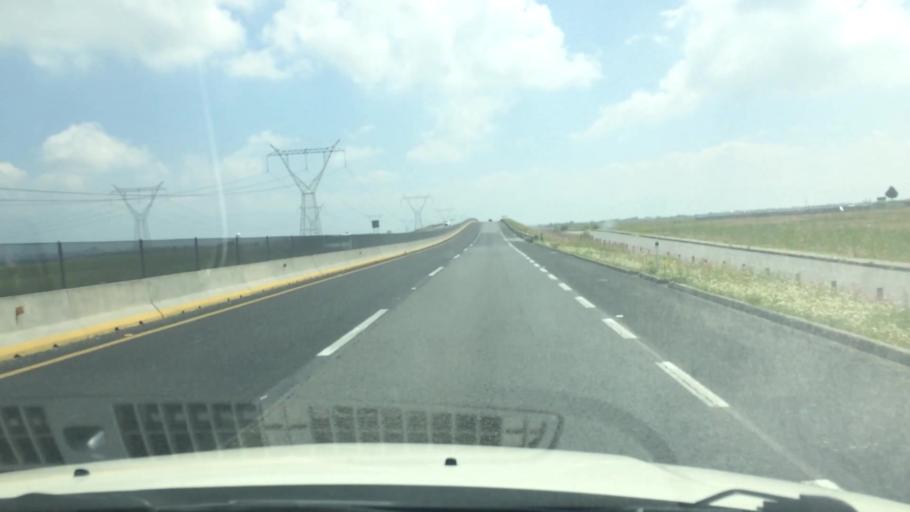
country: MX
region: Mexico
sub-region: Toluca
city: Barrio del Cajon
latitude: 19.3931
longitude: -99.6620
